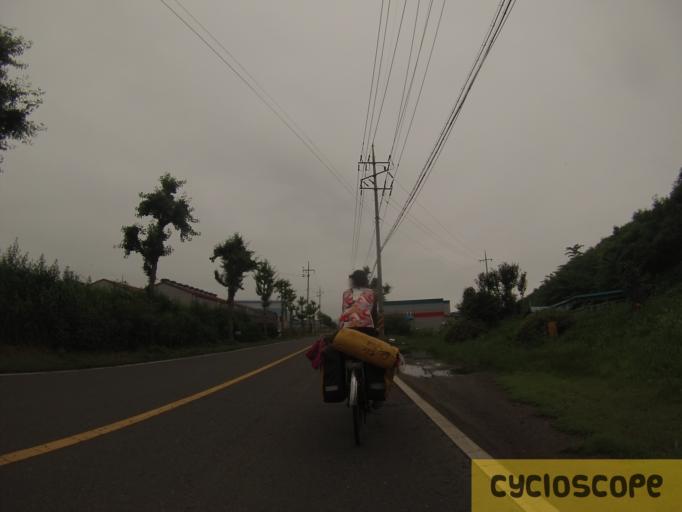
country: KR
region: Chungcheongnam-do
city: Taisen-ri
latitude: 36.2389
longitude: 126.5317
